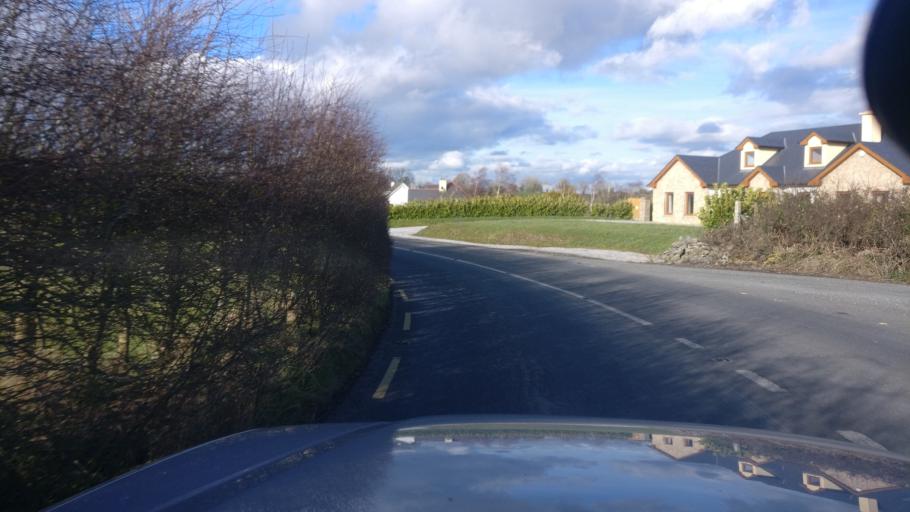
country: IE
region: Connaught
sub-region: County Galway
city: Loughrea
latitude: 53.1844
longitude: -8.3896
